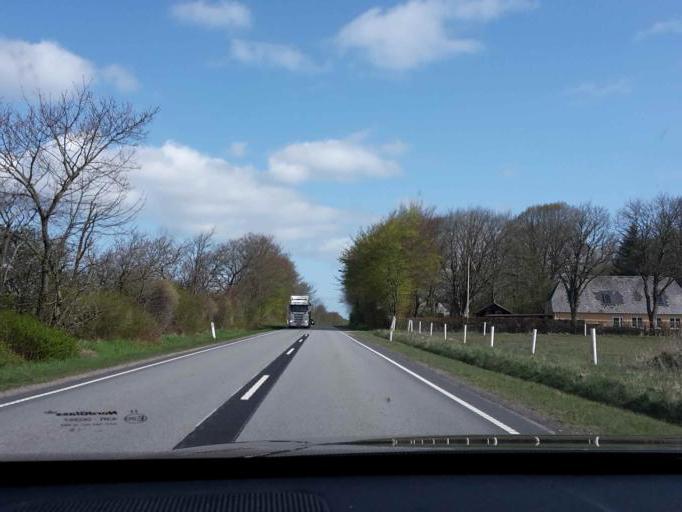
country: DK
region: South Denmark
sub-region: Vejen Kommune
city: Holsted
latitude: 55.6221
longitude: 8.9440
